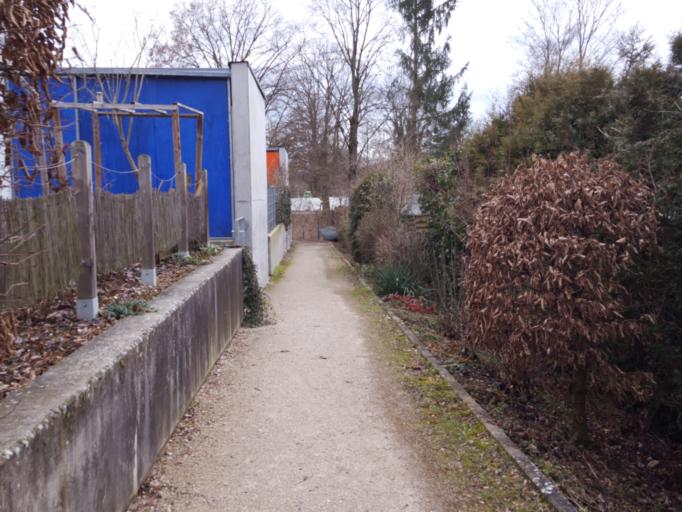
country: DE
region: Baden-Wuerttemberg
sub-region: Tuebingen Region
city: Tuebingen
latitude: 48.5109
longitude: 9.0361
